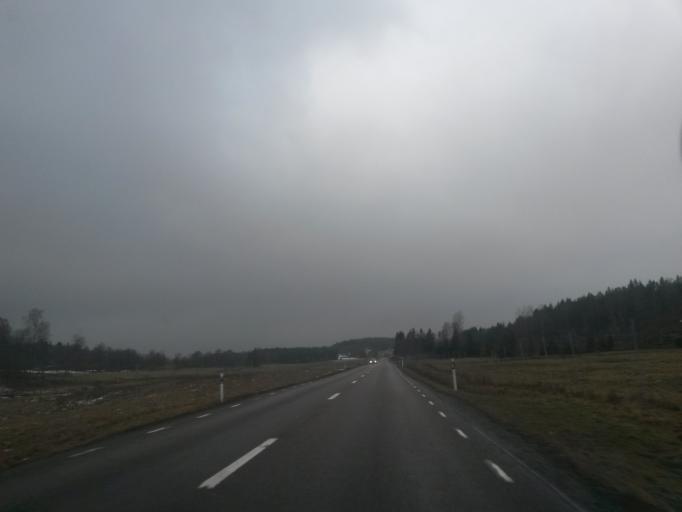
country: SE
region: Vaestra Goetaland
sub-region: Alingsas Kommun
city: Sollebrunn
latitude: 58.1370
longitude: 12.4411
